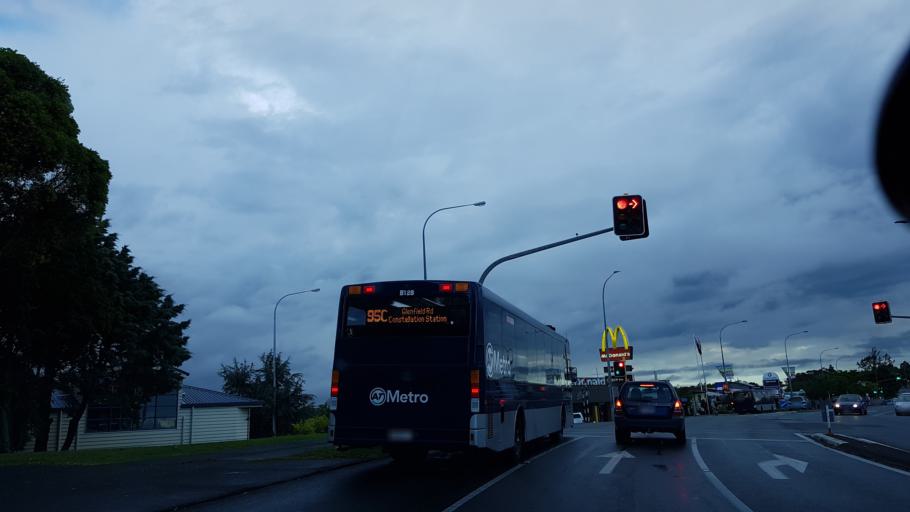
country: NZ
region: Auckland
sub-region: Auckland
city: North Shore
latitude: -36.7824
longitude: 174.7208
